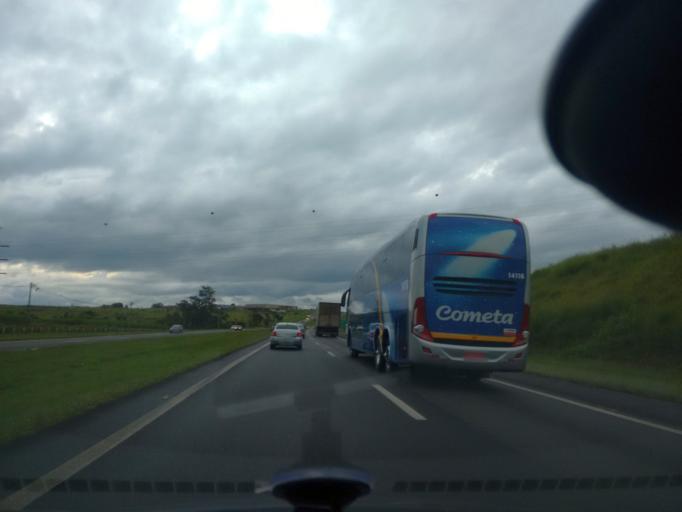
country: BR
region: Sao Paulo
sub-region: Santa Gertrudes
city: Santa Gertrudes
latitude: -22.4519
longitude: -47.5558
